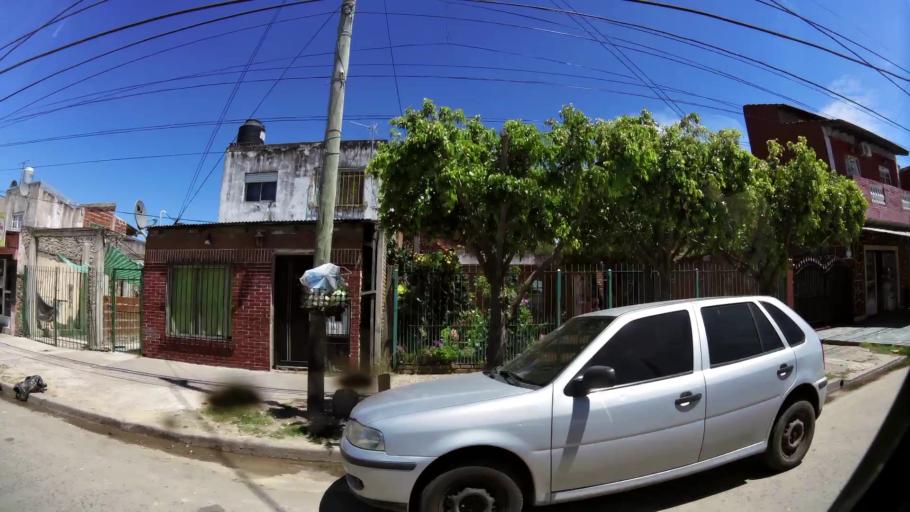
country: AR
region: Buenos Aires
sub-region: Partido de Quilmes
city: Quilmes
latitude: -34.7243
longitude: -58.3211
